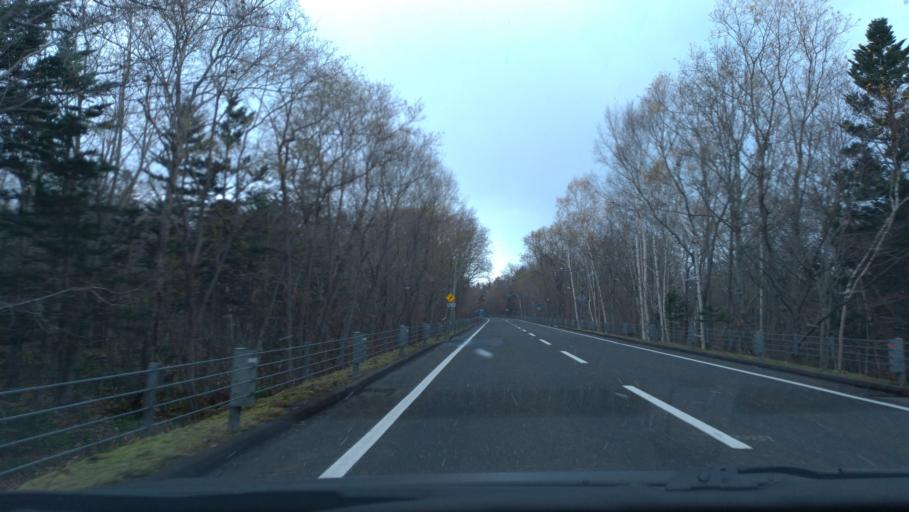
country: JP
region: Hokkaido
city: Shiraoi
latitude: 42.7403
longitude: 141.3876
